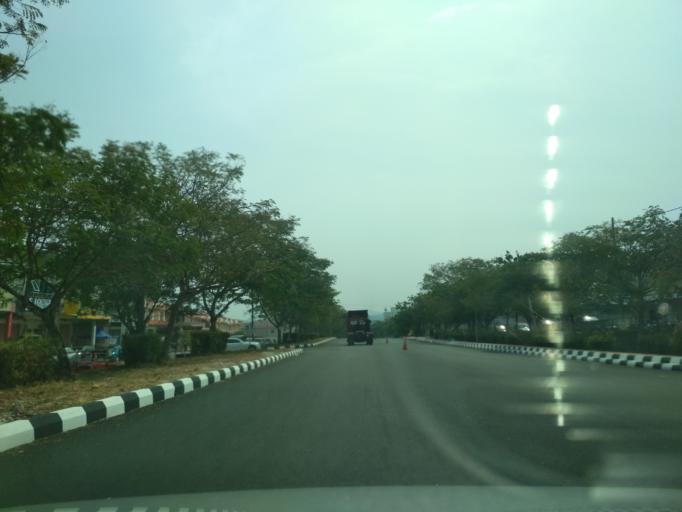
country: MY
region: Kedah
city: Kulim
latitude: 5.3707
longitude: 100.5659
